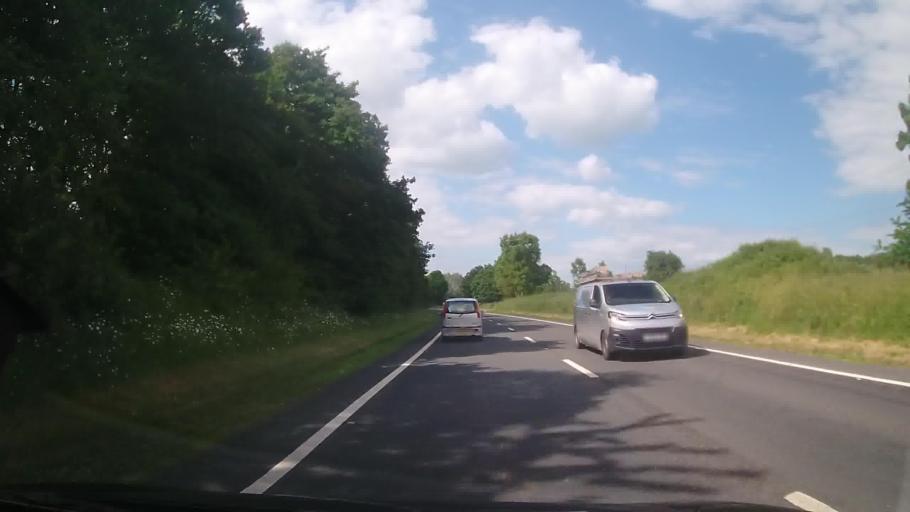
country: GB
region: England
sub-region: Herefordshire
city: Hope under Dinmore
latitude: 52.1852
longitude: -2.7159
